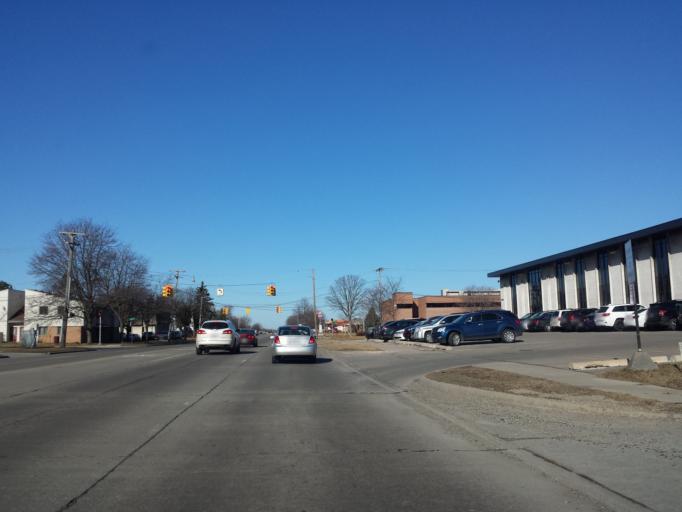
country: US
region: Michigan
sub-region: Oakland County
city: Lathrup Village
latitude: 42.5028
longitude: -83.2114
